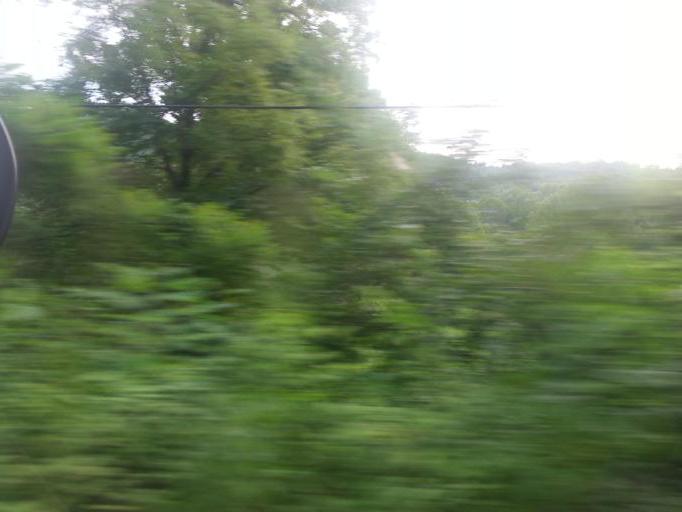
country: US
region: Tennessee
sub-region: Campbell County
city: Caryville
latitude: 36.2064
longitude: -84.3084
